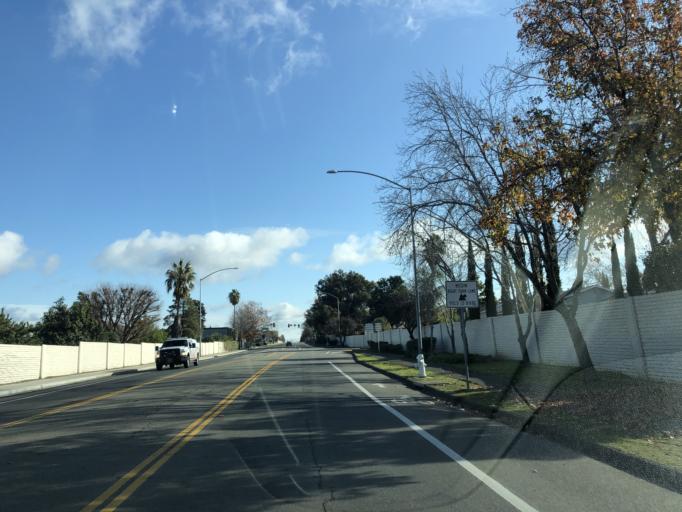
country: US
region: California
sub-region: Contra Costa County
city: Pittsburg
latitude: 37.9980
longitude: -121.8763
